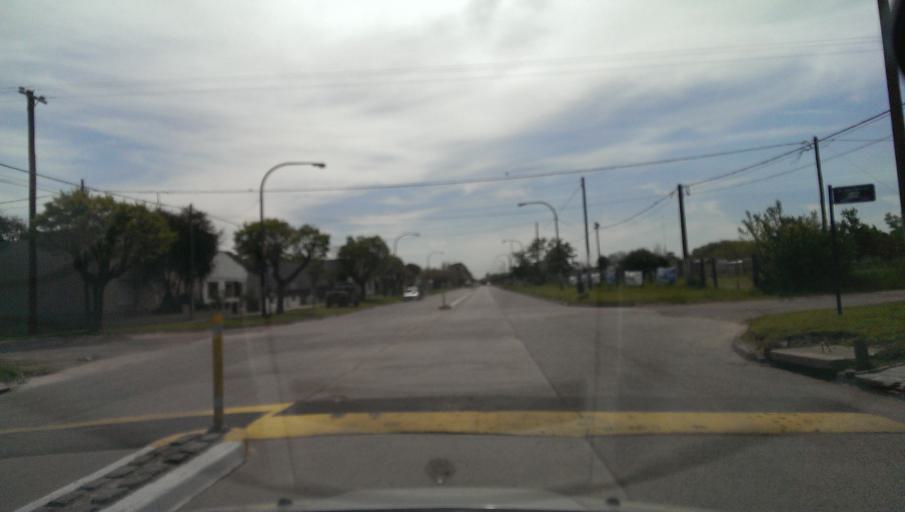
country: AR
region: Buenos Aires
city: Tapalque
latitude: -36.3844
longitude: -59.4968
